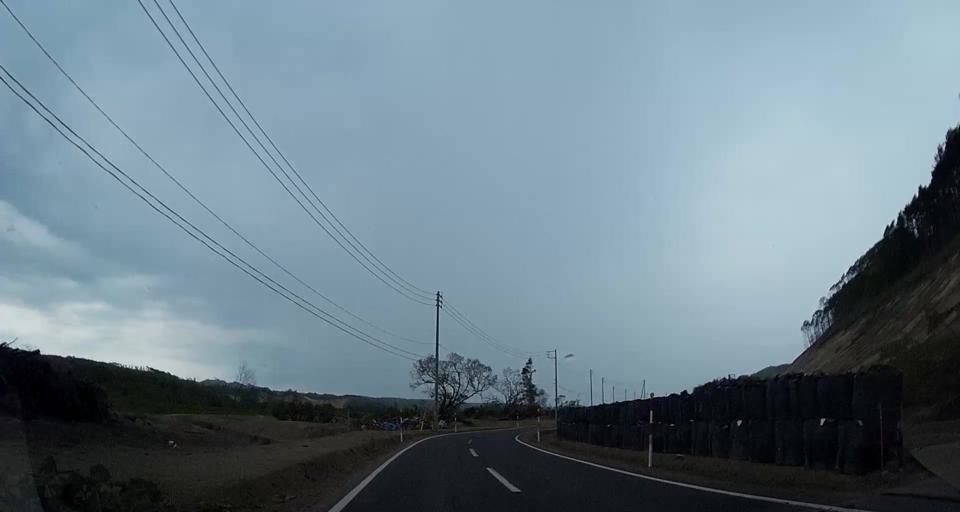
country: JP
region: Hokkaido
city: Chitose
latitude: 42.7538
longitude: 141.9156
